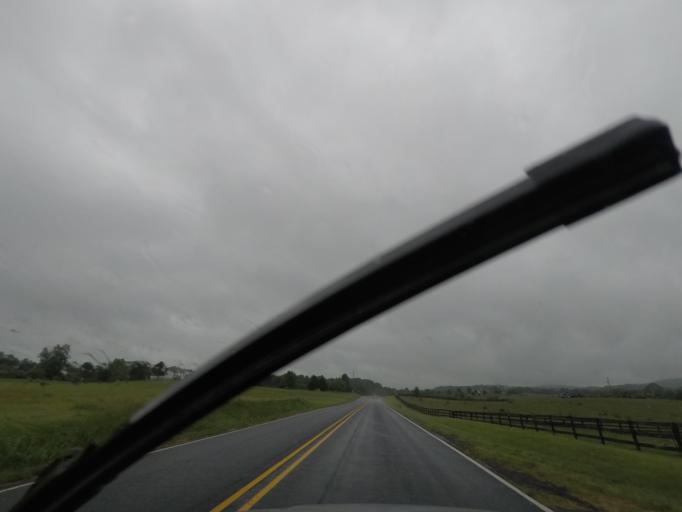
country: US
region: Virginia
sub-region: Culpeper County
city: Merrimac
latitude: 38.3559
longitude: -78.1113
